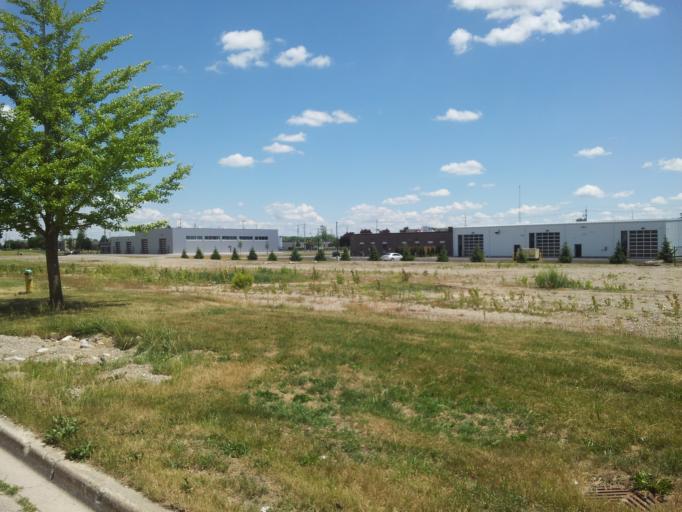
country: CA
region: Ontario
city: Stratford
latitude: 43.3685
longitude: -80.9606
